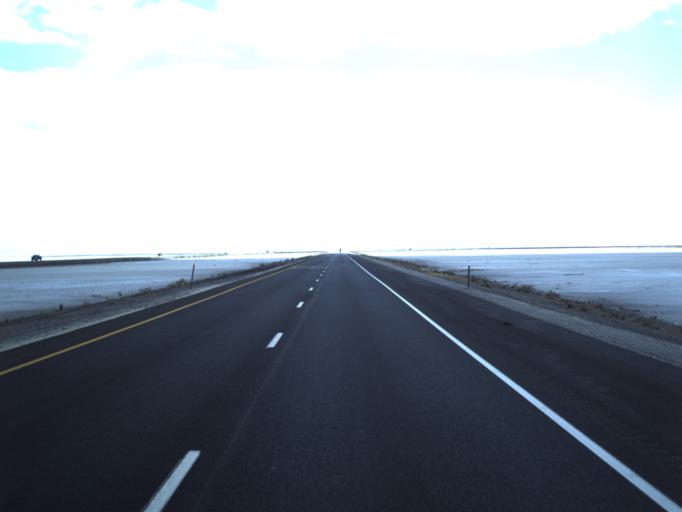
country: US
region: Utah
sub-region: Tooele County
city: Wendover
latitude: 40.7315
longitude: -113.5279
